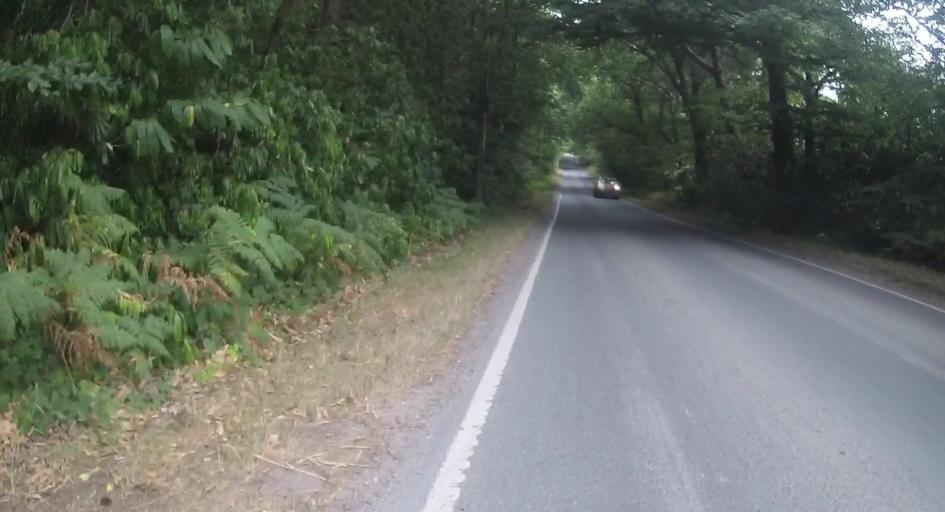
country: GB
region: England
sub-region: Dorset
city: Wareham
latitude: 50.6548
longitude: -2.1173
